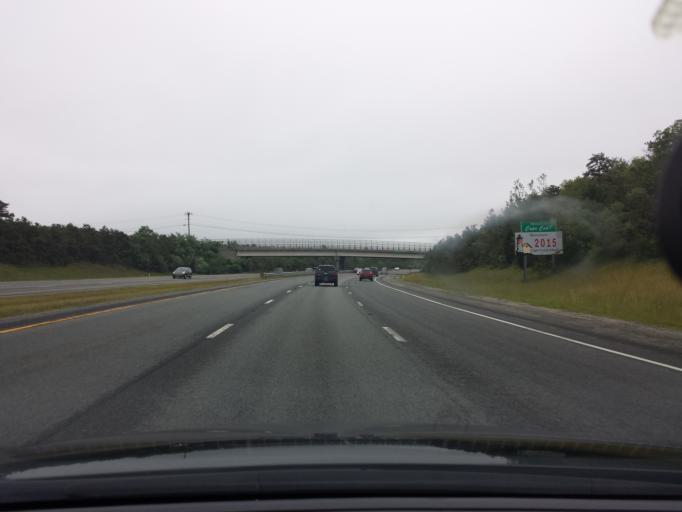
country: US
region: Massachusetts
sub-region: Barnstable County
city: Bourne
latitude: 41.7758
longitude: -70.5873
